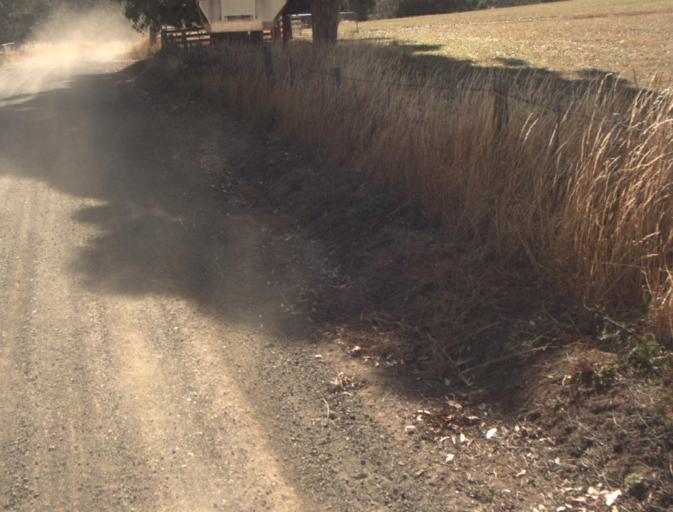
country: AU
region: Tasmania
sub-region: Dorset
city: Bridport
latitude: -41.1467
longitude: 147.2198
